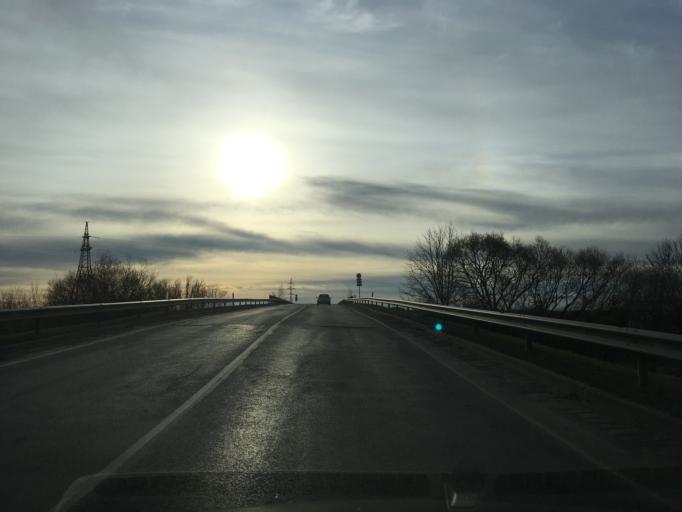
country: EE
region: Ida-Virumaa
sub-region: Narva linn
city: Narva
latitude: 59.3729
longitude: 28.1549
